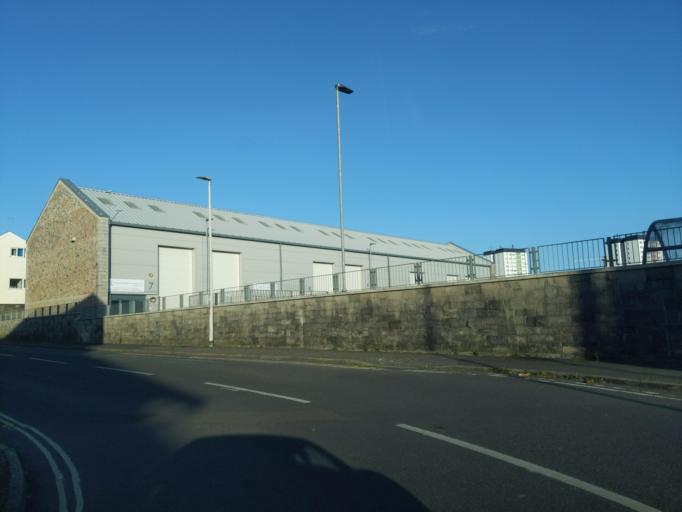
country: GB
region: England
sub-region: Cornwall
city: Millbrook
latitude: 50.3721
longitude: -4.1807
